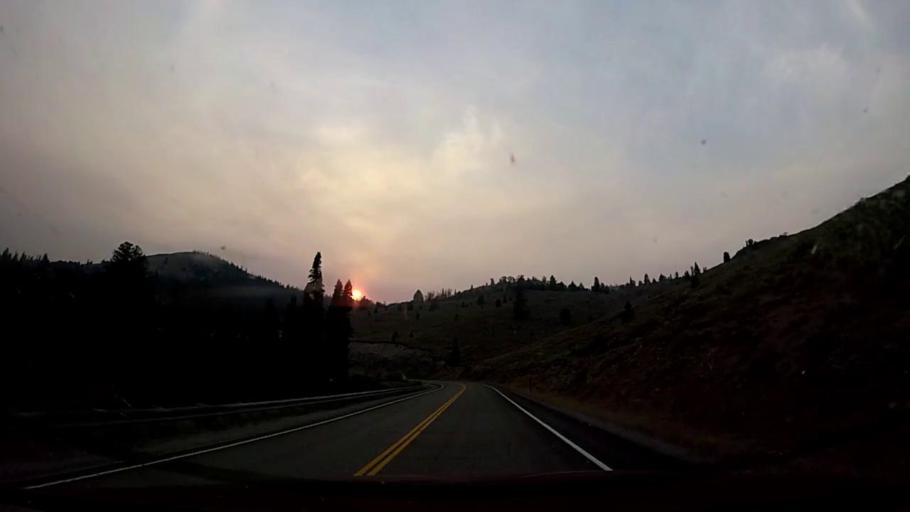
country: US
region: Idaho
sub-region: Blaine County
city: Ketchum
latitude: 43.8823
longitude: -114.6987
